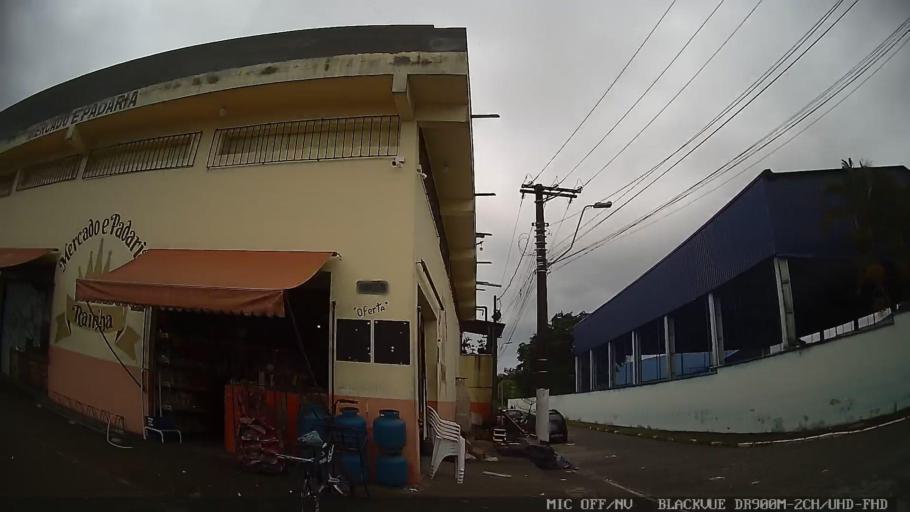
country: BR
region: Sao Paulo
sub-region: Sao Sebastiao
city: Sao Sebastiao
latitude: -23.7077
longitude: -45.4435
